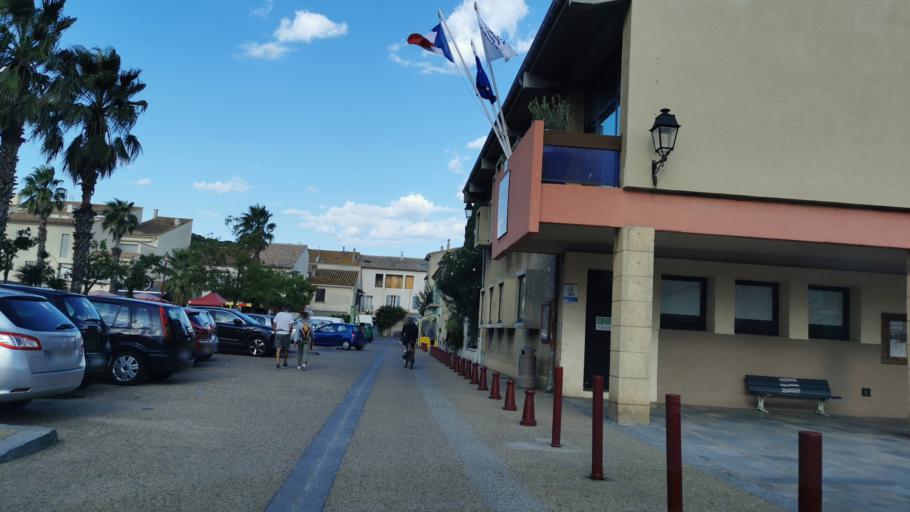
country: FR
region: Languedoc-Roussillon
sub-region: Departement de l'Aude
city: Gruissan
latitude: 43.1058
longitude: 3.0867
